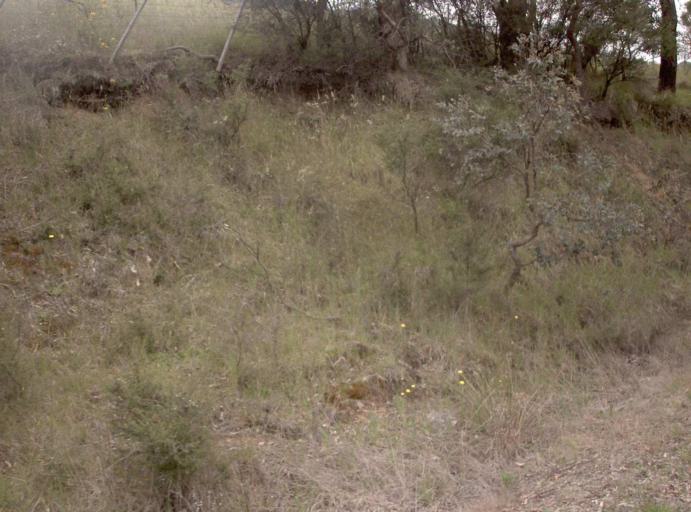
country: AU
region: Victoria
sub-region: East Gippsland
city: Bairnsdale
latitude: -37.5837
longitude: 147.1833
